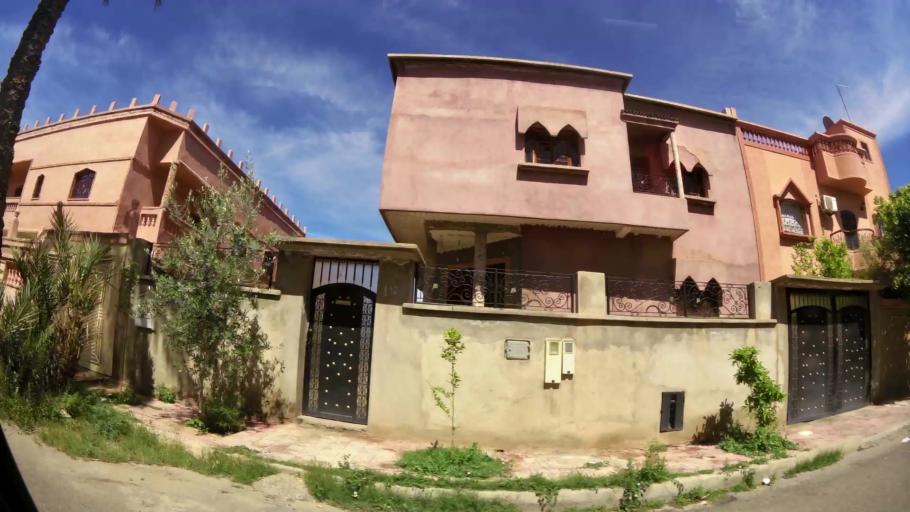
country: MA
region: Marrakech-Tensift-Al Haouz
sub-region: Marrakech
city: Marrakesh
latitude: 31.6661
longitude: -7.9939
